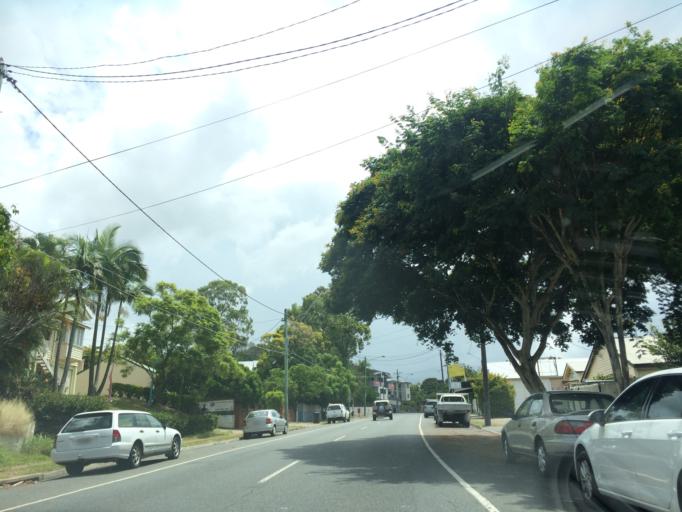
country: AU
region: Queensland
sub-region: Brisbane
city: Morningside
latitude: -27.4722
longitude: 153.0622
